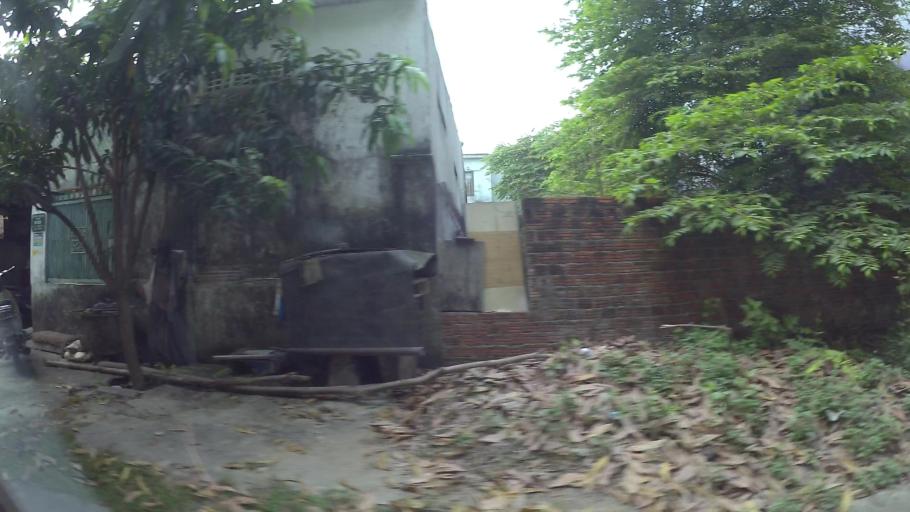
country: VN
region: Da Nang
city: Lien Chieu
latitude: 16.0583
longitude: 108.1611
